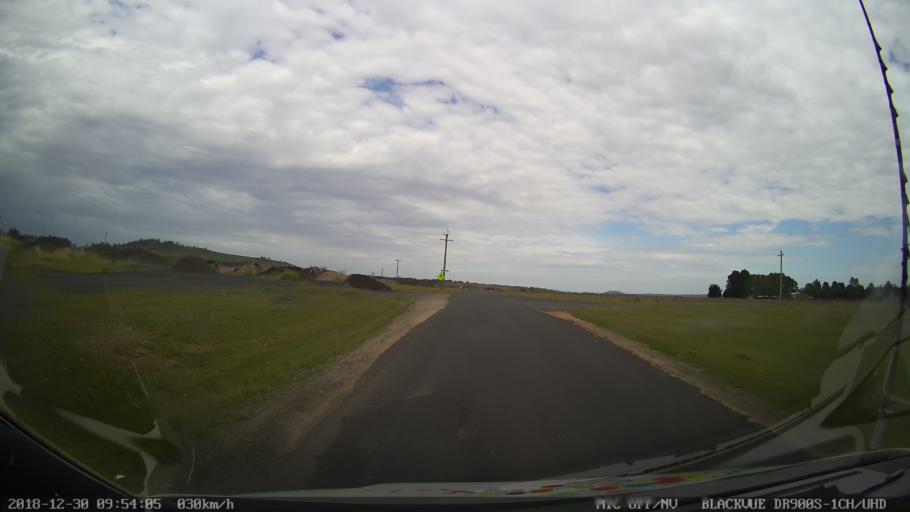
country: AU
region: New South Wales
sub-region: Cooma-Monaro
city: Cooma
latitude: -36.5185
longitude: 149.2806
